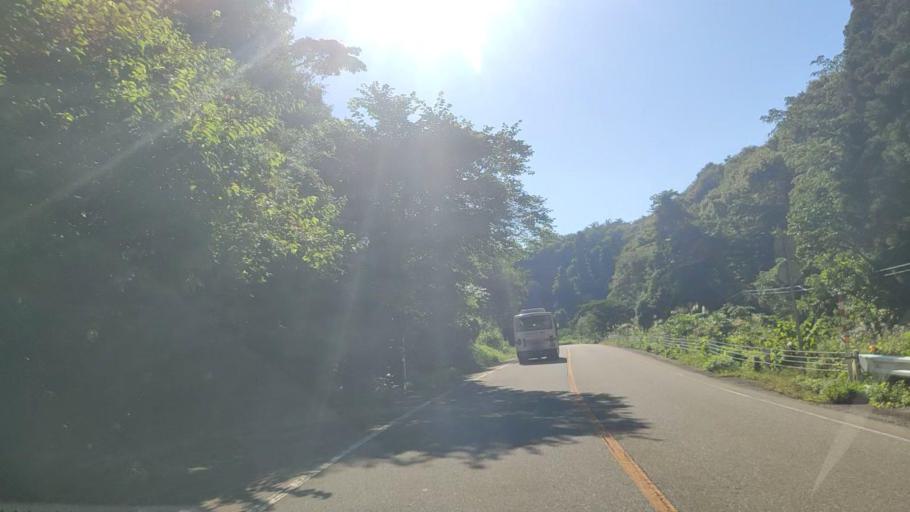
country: JP
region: Ishikawa
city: Nanao
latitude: 37.2446
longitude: 136.9902
